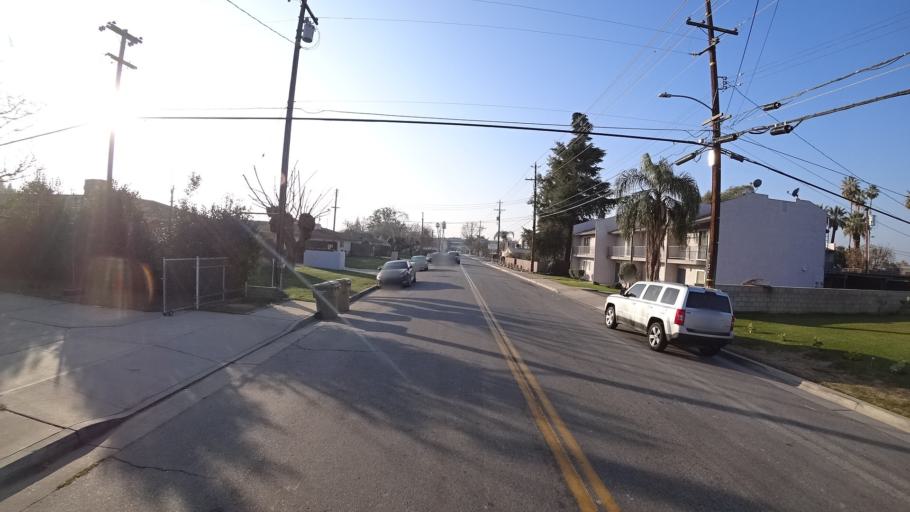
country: US
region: California
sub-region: Kern County
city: Bakersfield
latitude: 35.3561
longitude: -119.0459
